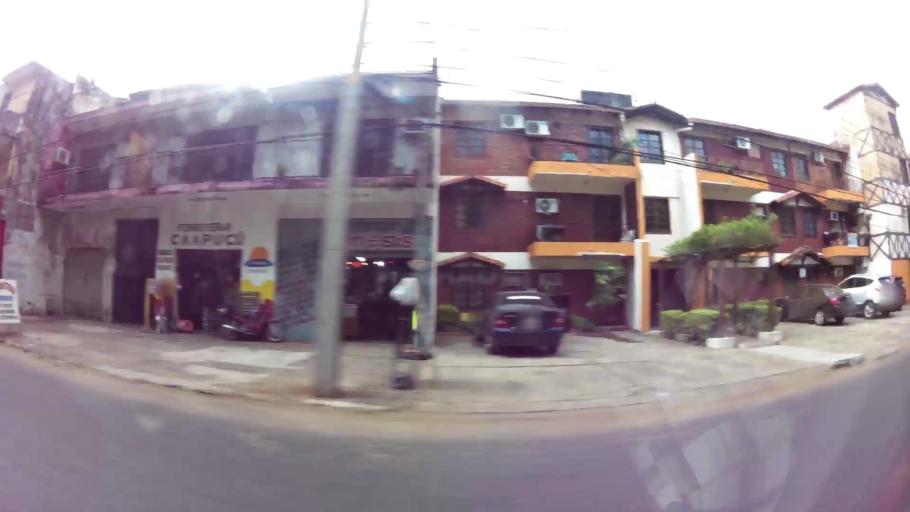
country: PY
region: Central
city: Villa Elisa
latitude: -25.3403
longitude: -57.5647
